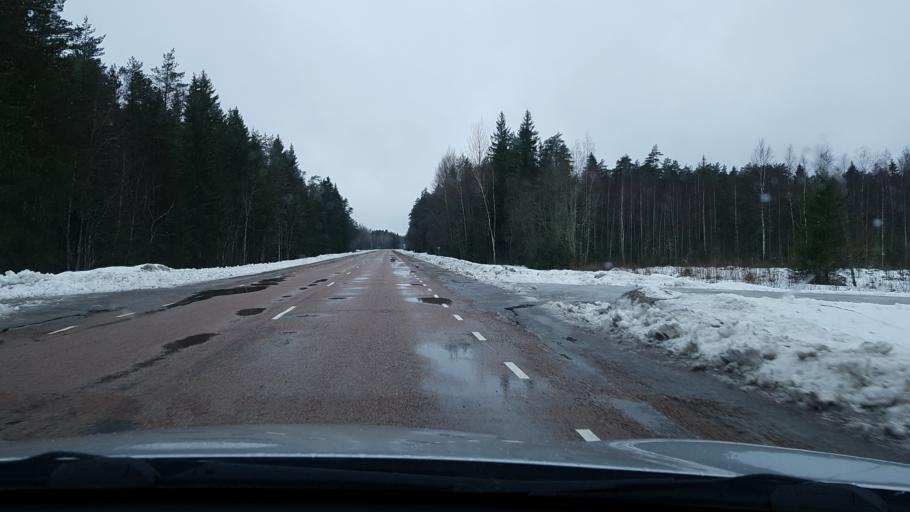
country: EE
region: Vorumaa
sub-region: Voru linn
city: Voru
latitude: 57.7584
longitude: 26.8395
